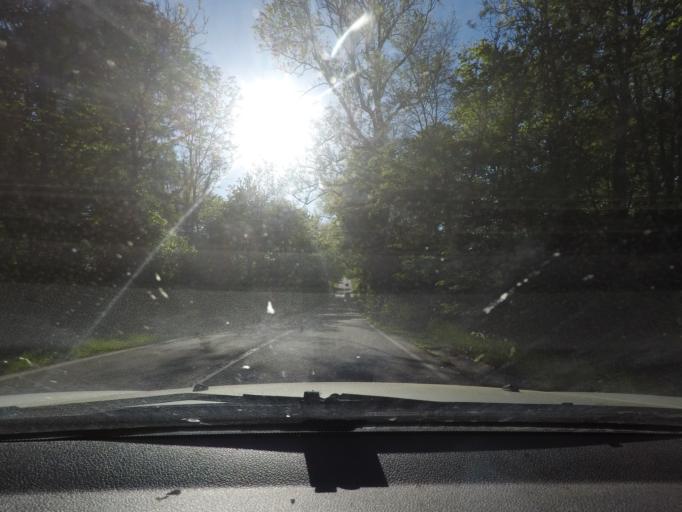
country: BE
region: Wallonia
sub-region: Province du Luxembourg
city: Wellin
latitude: 50.1675
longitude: 5.0953
